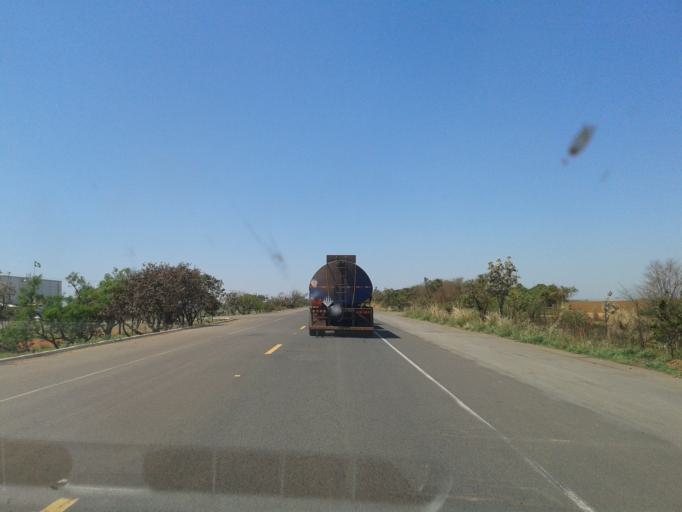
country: BR
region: Minas Gerais
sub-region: Araxa
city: Araxa
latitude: -19.3131
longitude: -47.3892
